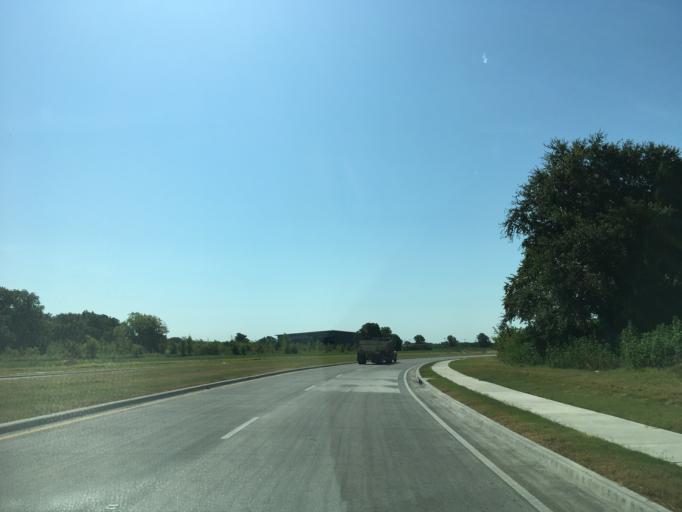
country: US
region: Texas
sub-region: Collin County
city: Fairview
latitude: 33.1702
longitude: -96.6060
